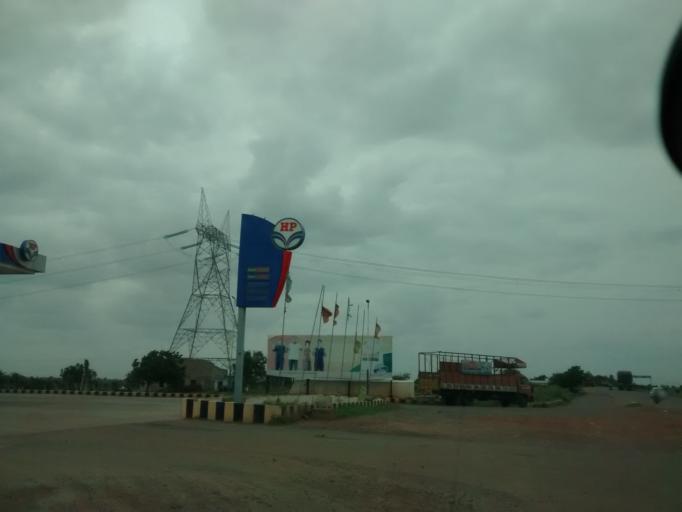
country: IN
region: Telangana
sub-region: Mahbubnagar
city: Alampur
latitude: 15.7227
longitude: 78.0010
